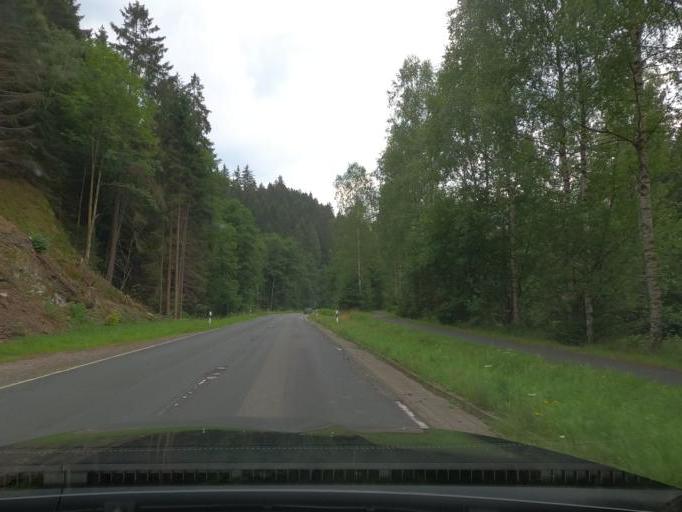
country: DE
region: Lower Saxony
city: Wildemann
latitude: 51.8508
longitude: 10.2735
